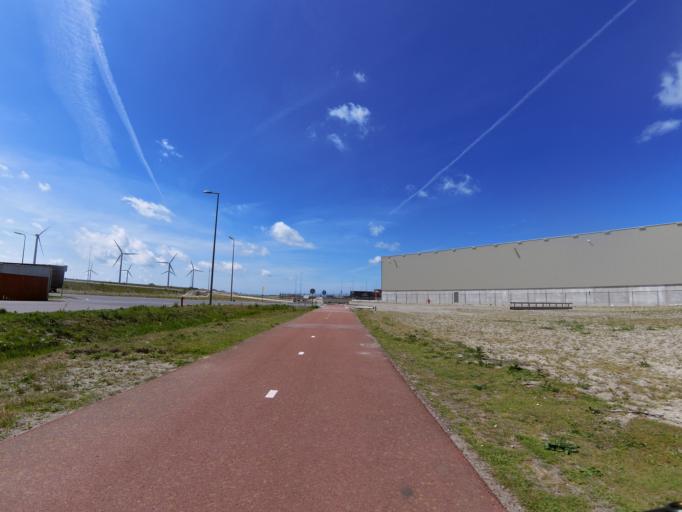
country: NL
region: South Holland
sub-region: Gemeente Rotterdam
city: Hoek van Holland
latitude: 51.9353
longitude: 4.0210
